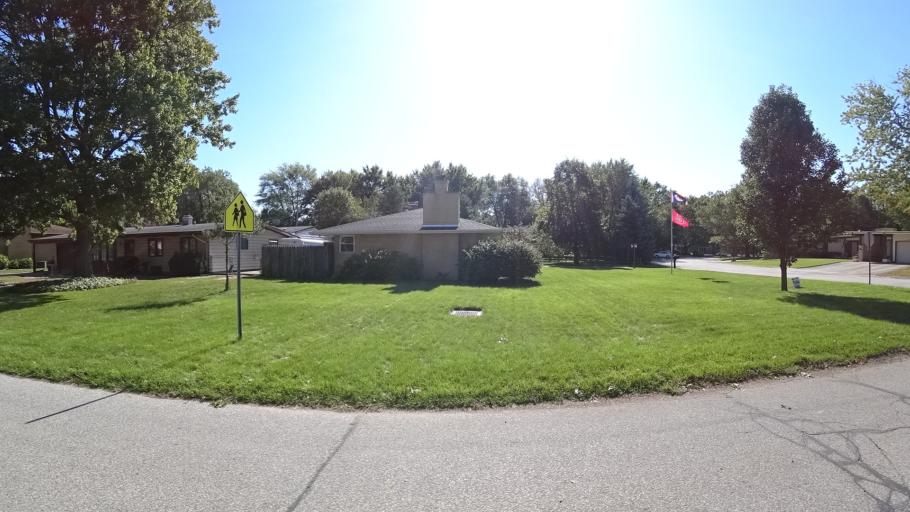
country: US
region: Indiana
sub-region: LaPorte County
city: Michigan City
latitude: 41.6916
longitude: -86.8887
